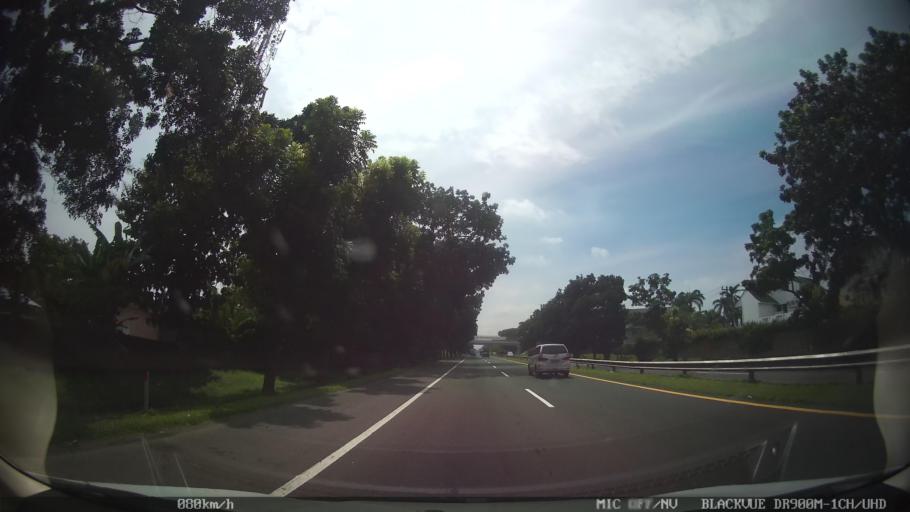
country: ID
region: North Sumatra
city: Medan
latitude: 3.6424
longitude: 98.6946
